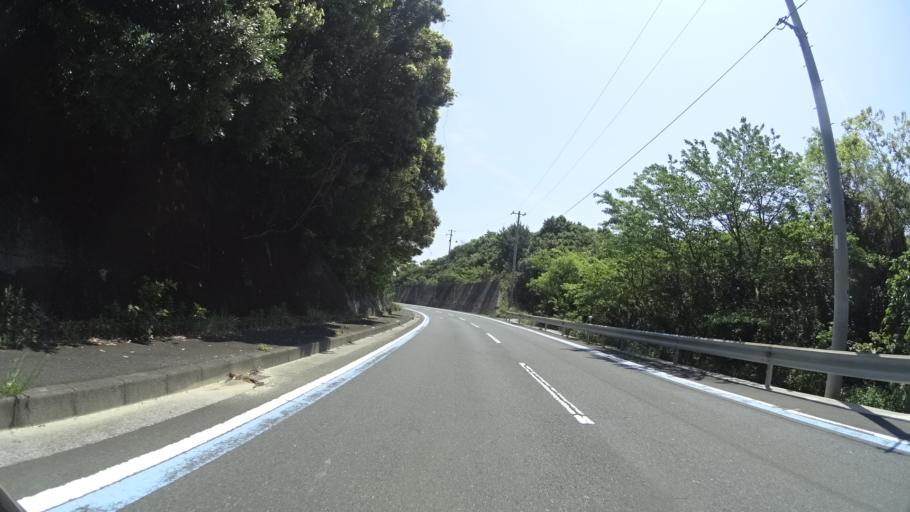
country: JP
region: Ehime
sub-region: Nishiuwa-gun
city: Ikata-cho
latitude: 33.4405
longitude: 132.2425
